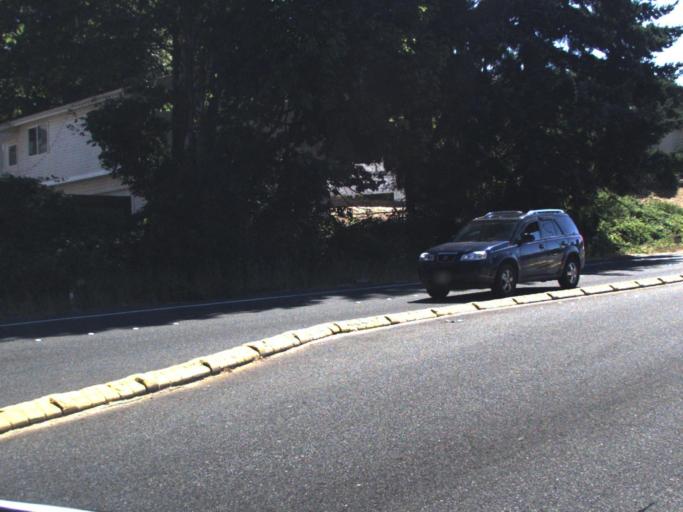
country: US
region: Washington
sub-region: King County
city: Renton
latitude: 47.5015
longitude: -122.1865
